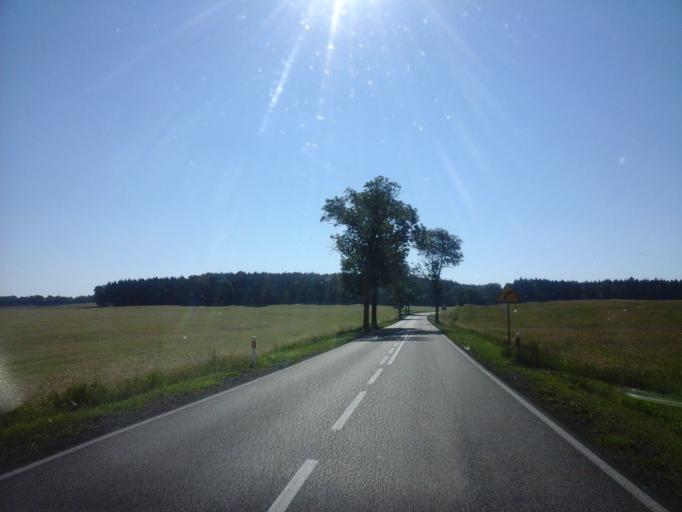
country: PL
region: West Pomeranian Voivodeship
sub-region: Powiat drawski
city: Drawsko Pomorskie
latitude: 53.4967
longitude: 15.6900
